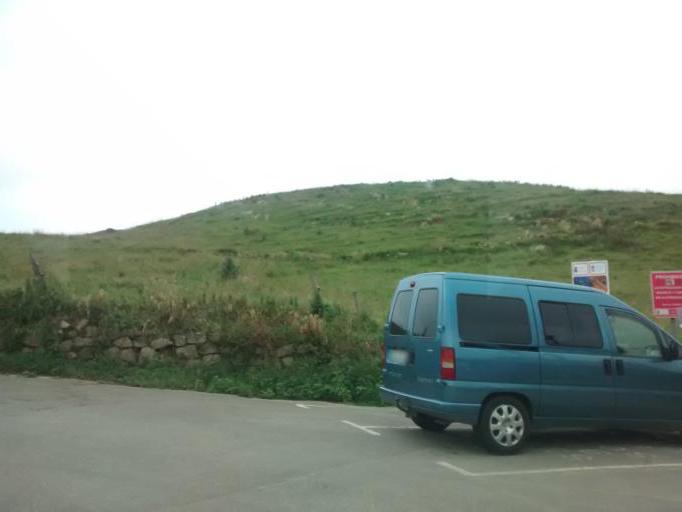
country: ES
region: Cantabria
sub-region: Provincia de Cantabria
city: Santillana
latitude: 43.4230
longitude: -4.0991
